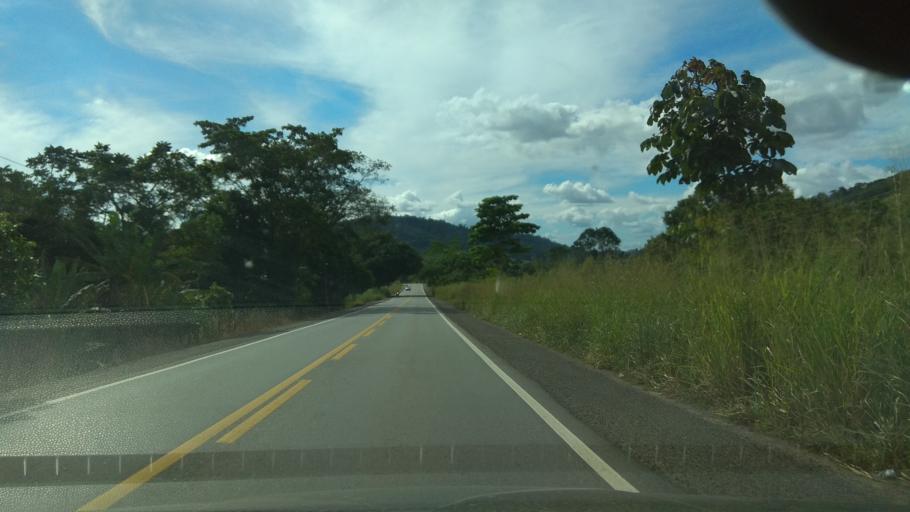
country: BR
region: Bahia
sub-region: Jitauna
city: Jitauna
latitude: -14.0282
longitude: -39.8326
